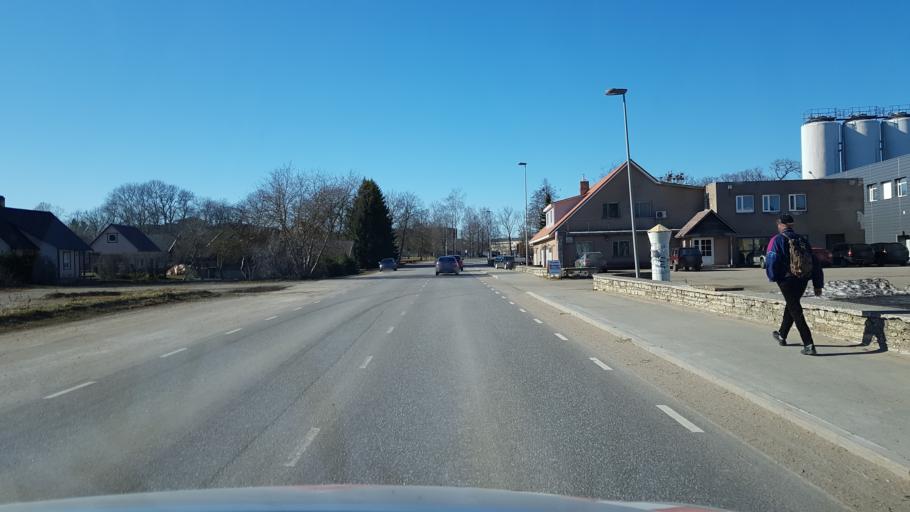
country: EE
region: Laeaene-Virumaa
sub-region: Haljala vald
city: Haljala
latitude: 59.4289
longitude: 26.2679
